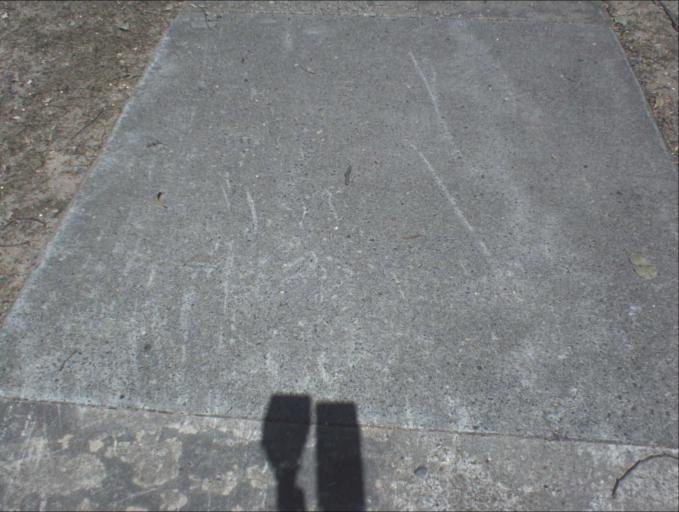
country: AU
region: Queensland
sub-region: Logan
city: Springwood
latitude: -27.6004
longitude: 153.1463
